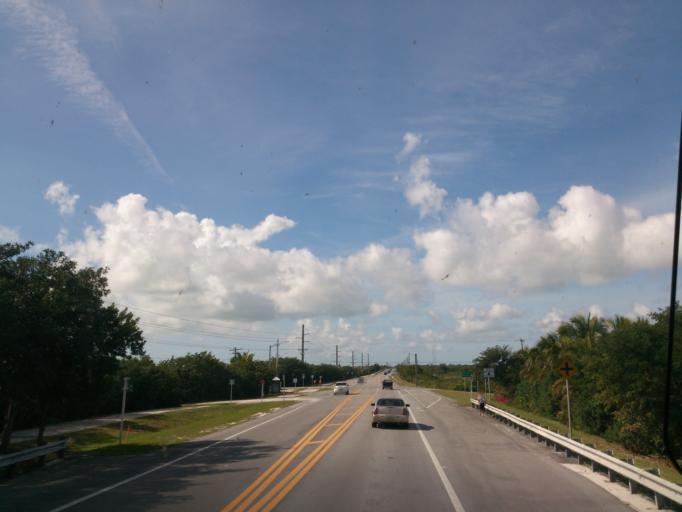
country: US
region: Florida
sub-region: Monroe County
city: Big Pine Key
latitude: 24.6666
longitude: -81.3864
